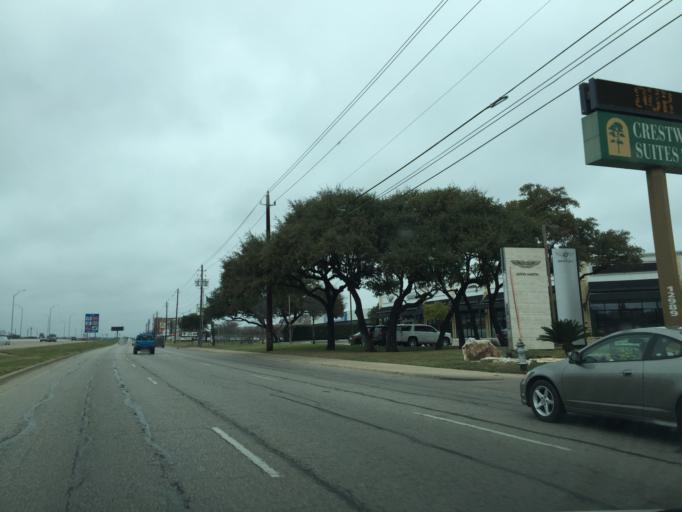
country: US
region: Texas
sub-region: Williamson County
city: Jollyville
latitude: 30.4379
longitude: -97.7761
